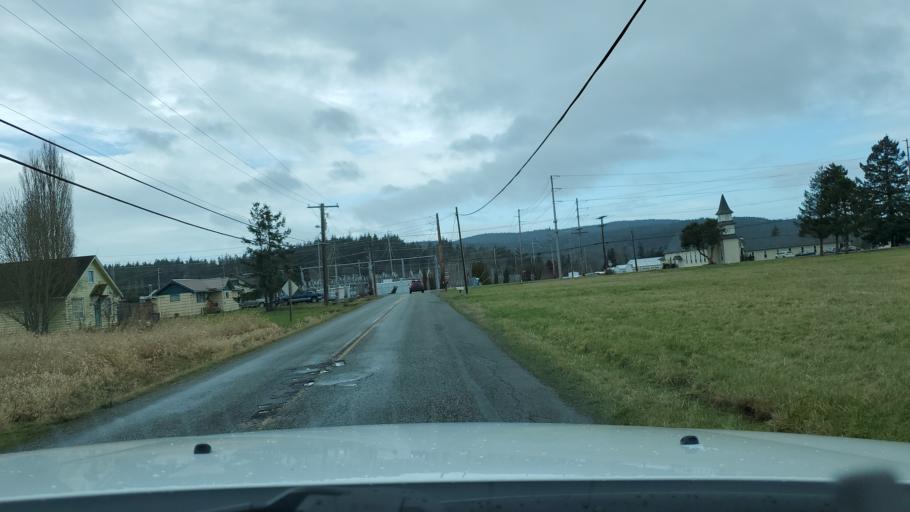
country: US
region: Washington
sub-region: Skagit County
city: Anacortes
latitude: 48.4585
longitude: -122.5583
